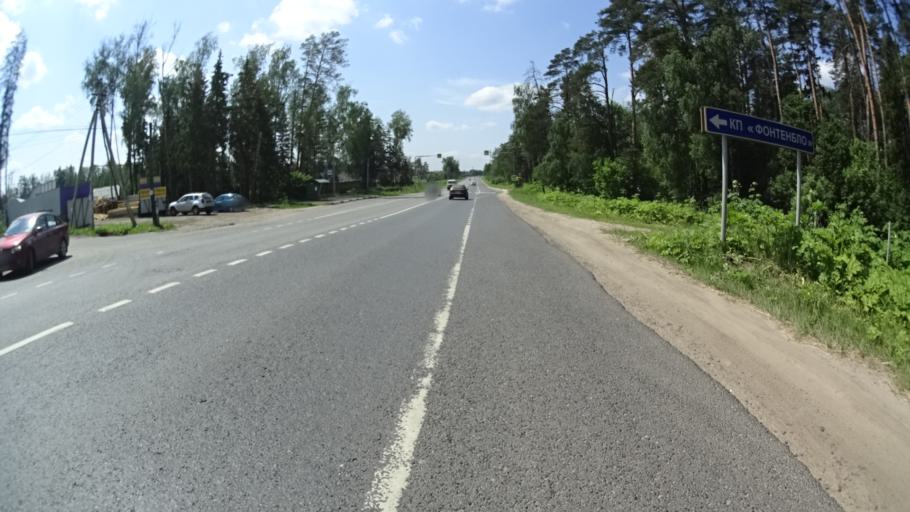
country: RU
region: Moskovskaya
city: Lesnoy
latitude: 56.0582
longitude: 38.0058
